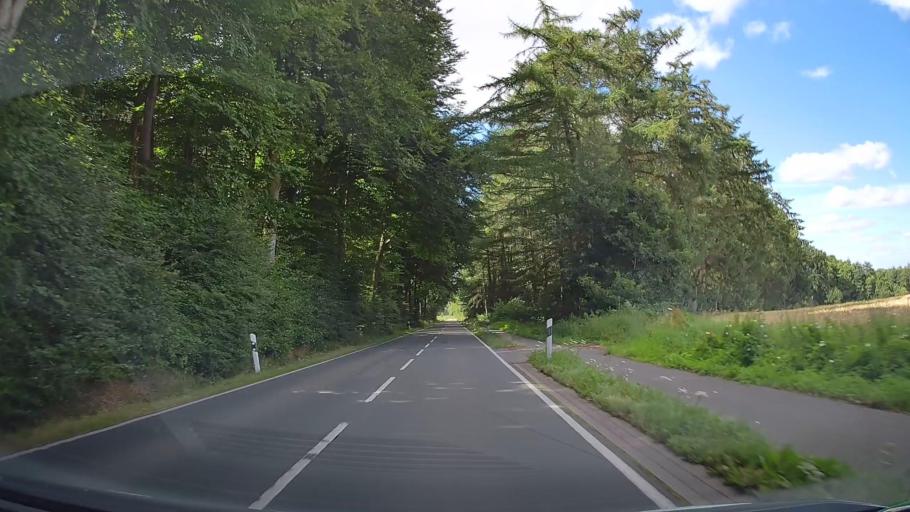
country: DE
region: Lower Saxony
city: Ankum
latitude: 52.5195
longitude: 7.9001
